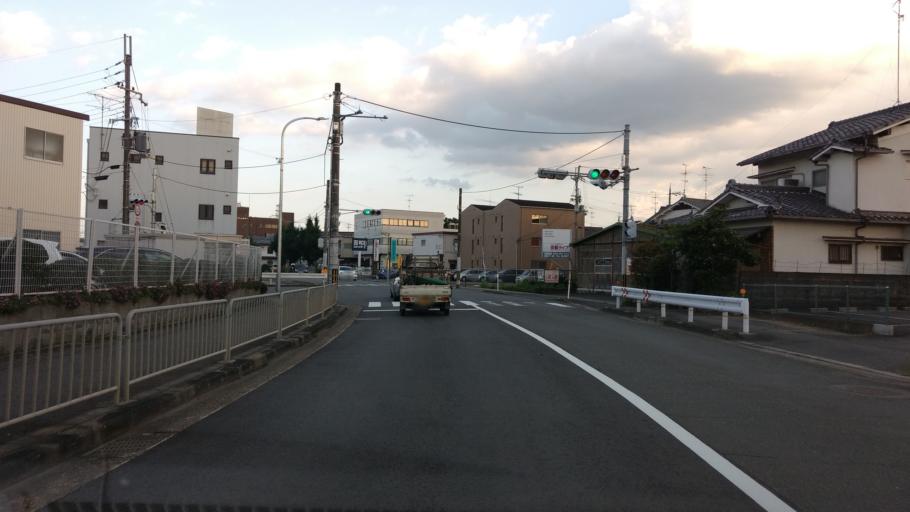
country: JP
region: Kyoto
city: Muko
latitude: 34.9633
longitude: 135.7265
